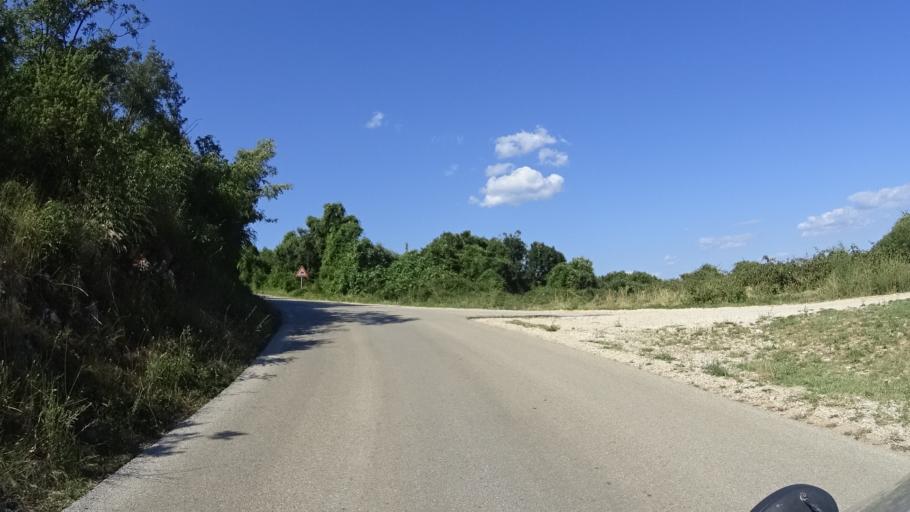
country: HR
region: Istarska
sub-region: Grad Labin
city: Rabac
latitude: 45.0061
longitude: 14.1618
